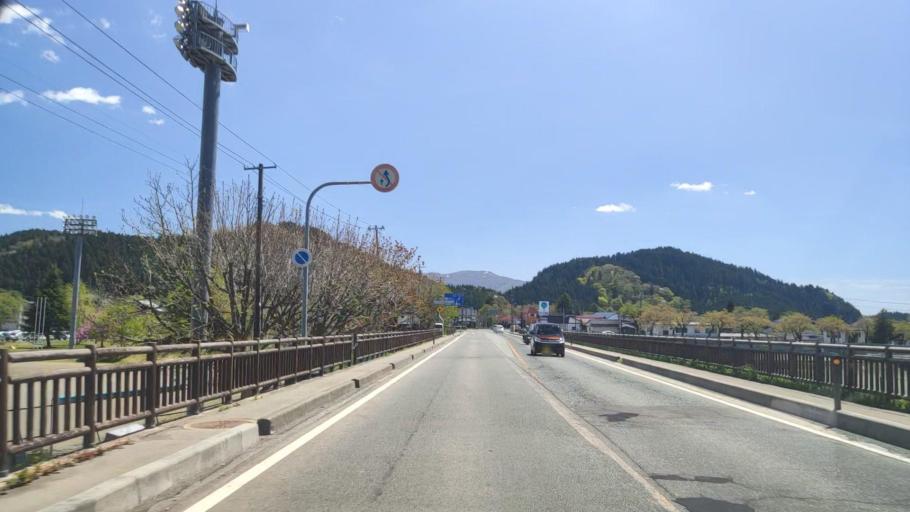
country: JP
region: Yamagata
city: Shinjo
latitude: 38.8851
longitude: 140.3350
